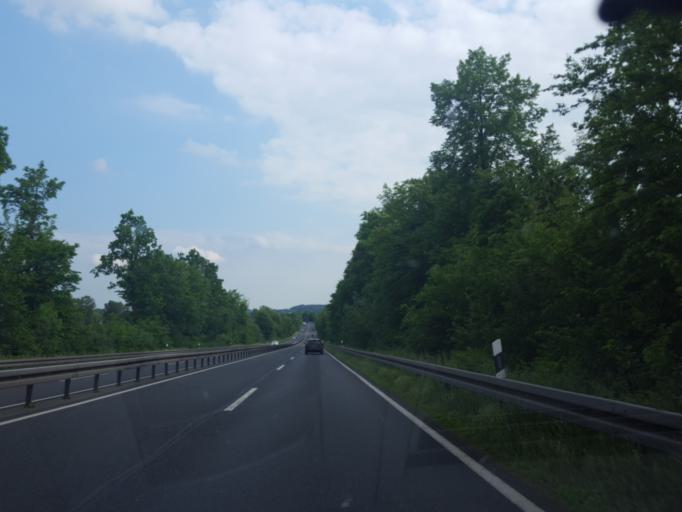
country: DE
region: Lower Saxony
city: Gittelde
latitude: 51.7952
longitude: 10.1962
